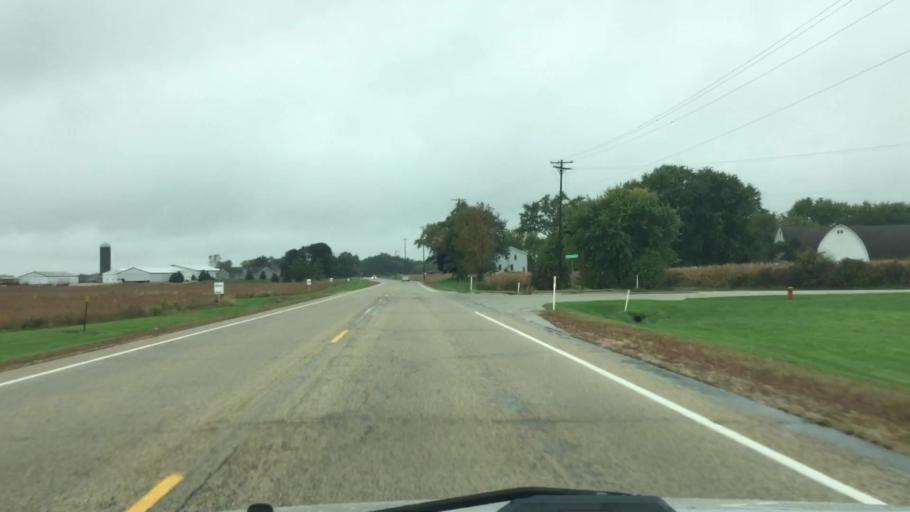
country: US
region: Wisconsin
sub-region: Jefferson County
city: Palmyra
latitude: 42.8789
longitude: -88.6297
